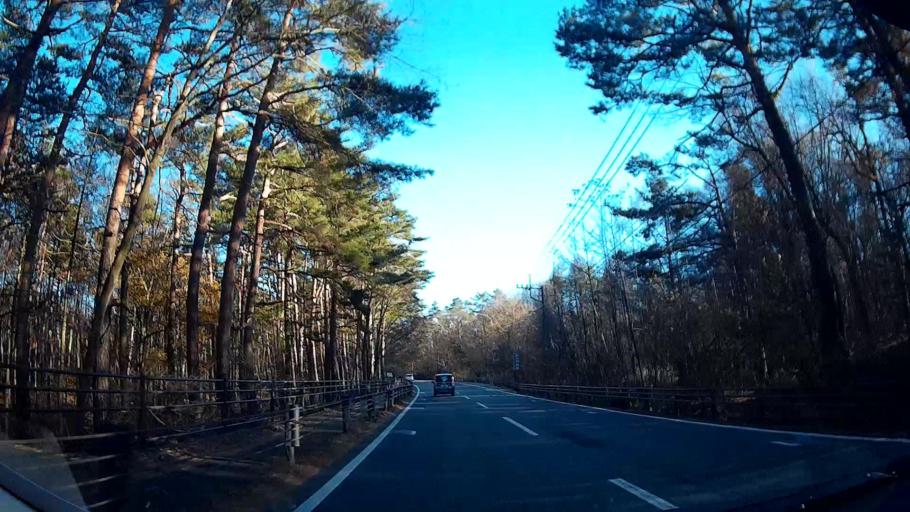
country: JP
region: Yamanashi
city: Fujikawaguchiko
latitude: 35.4511
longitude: 138.8143
